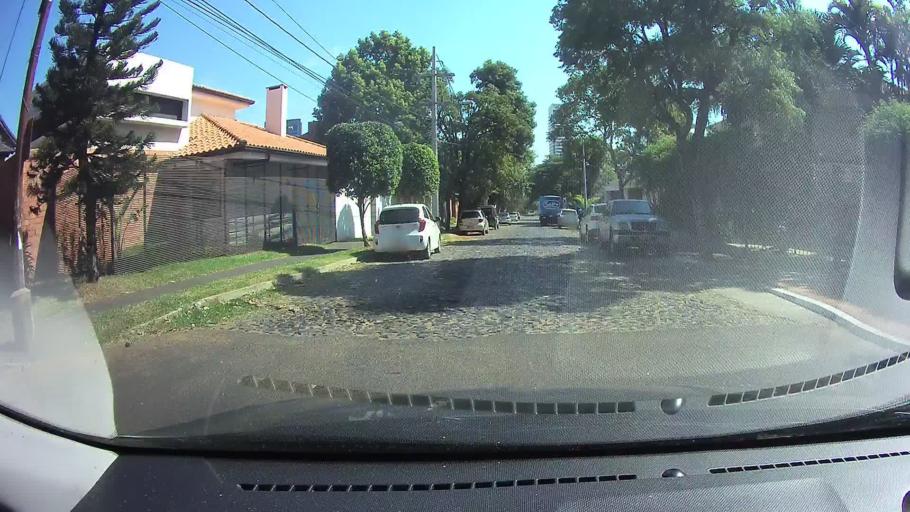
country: PY
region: Central
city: Fernando de la Mora
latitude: -25.2899
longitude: -57.5636
